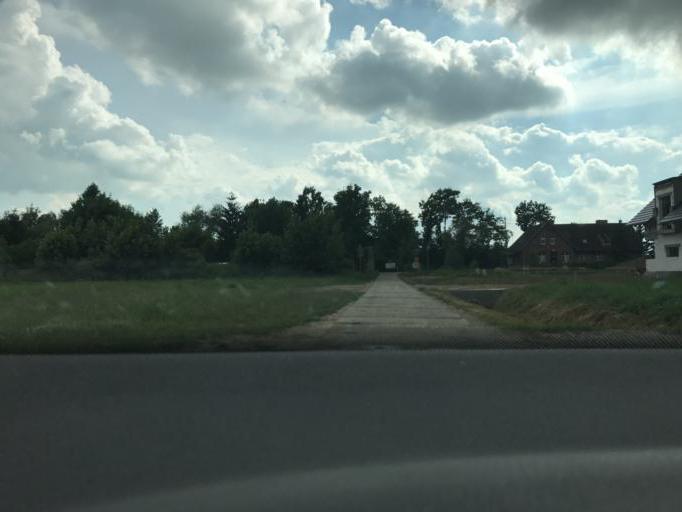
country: PL
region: Pomeranian Voivodeship
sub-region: Powiat gdanski
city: Cedry Wielkie
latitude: 54.3319
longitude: 18.8018
